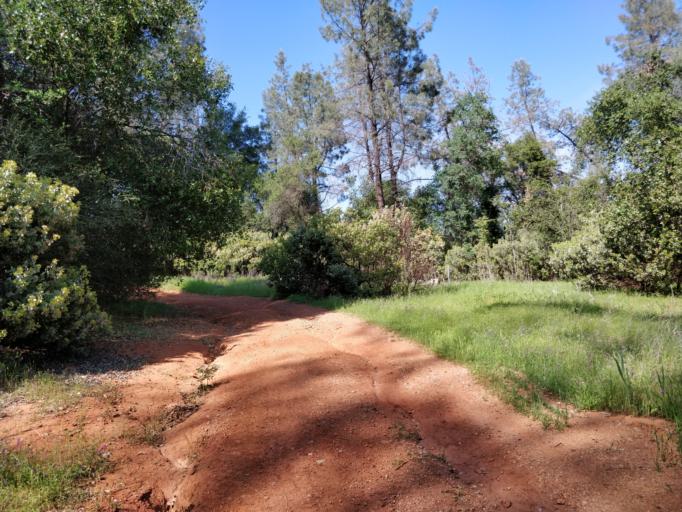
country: US
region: California
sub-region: Shasta County
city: Central Valley (historical)
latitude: 40.6672
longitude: -122.3716
